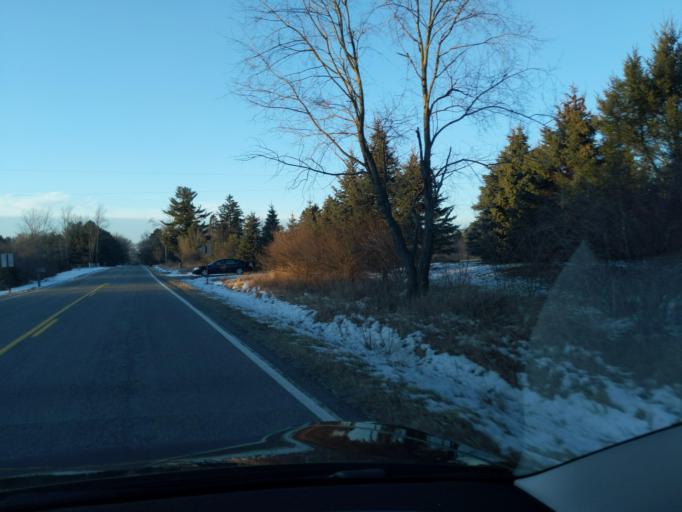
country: US
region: Michigan
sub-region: Ingham County
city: Stockbridge
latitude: 42.5207
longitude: -84.2720
